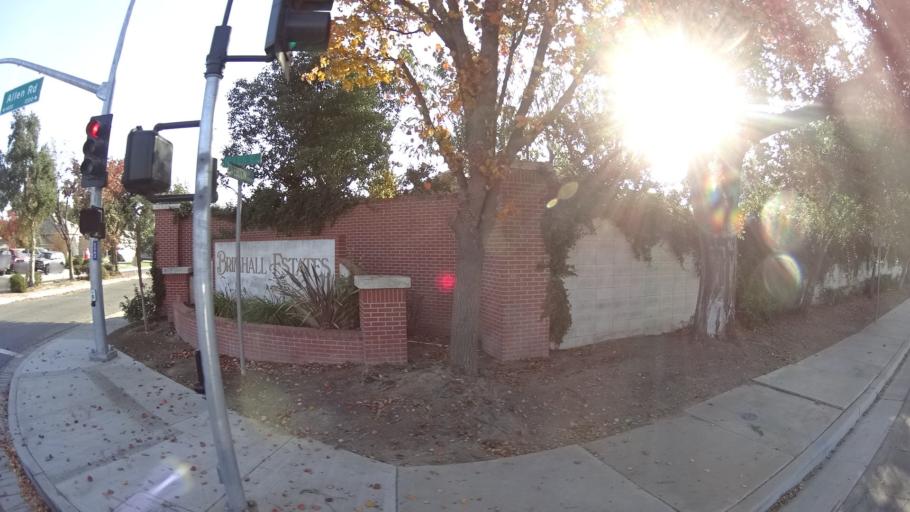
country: US
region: California
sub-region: Kern County
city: Rosedale
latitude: 35.3705
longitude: -119.1454
